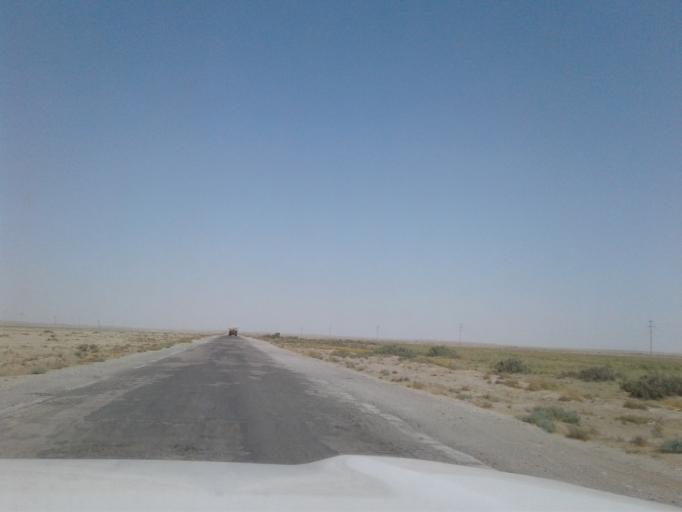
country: TM
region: Balkan
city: Gumdag
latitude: 38.3441
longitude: 54.3636
